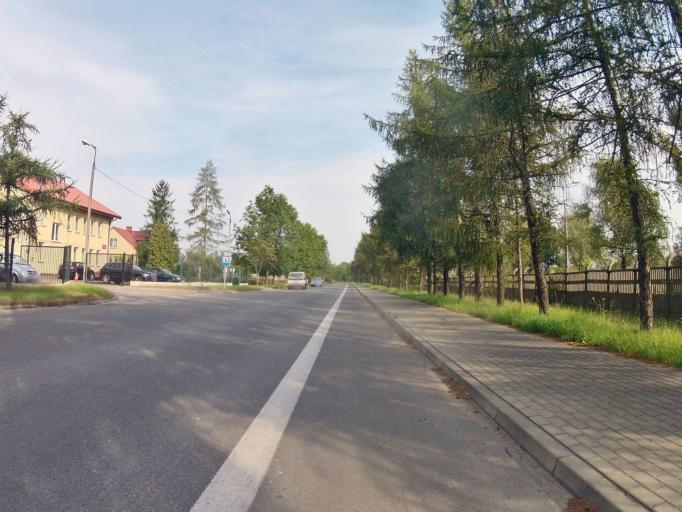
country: PL
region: Subcarpathian Voivodeship
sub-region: Powiat jasielski
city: Jaslo
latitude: 49.7219
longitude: 21.4504
